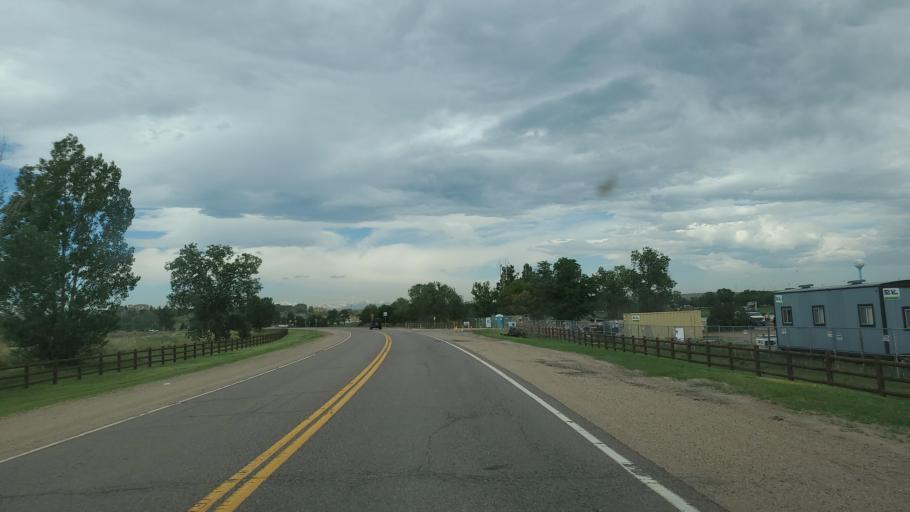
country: US
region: Colorado
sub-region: Adams County
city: Todd Creek
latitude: 39.9242
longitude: -104.8703
